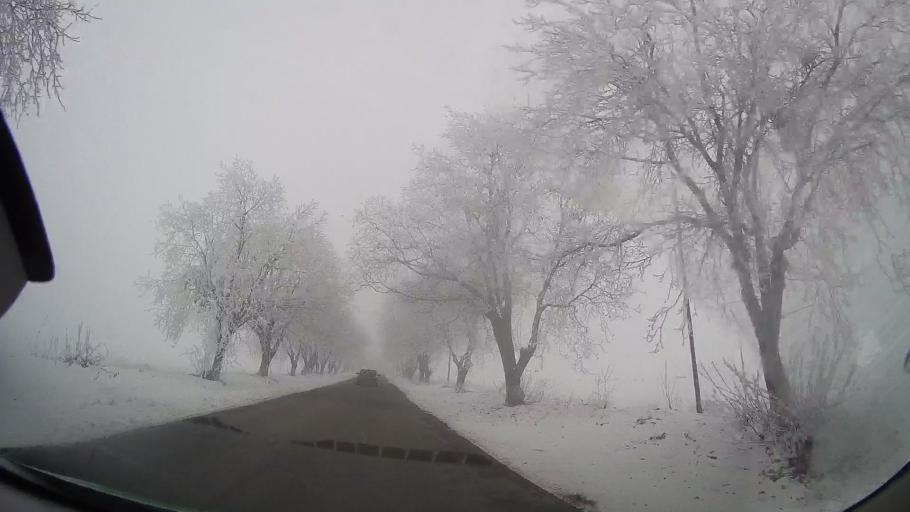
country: RO
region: Neamt
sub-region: Comuna Cordun
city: Cordun
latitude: 46.9840
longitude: 26.8645
